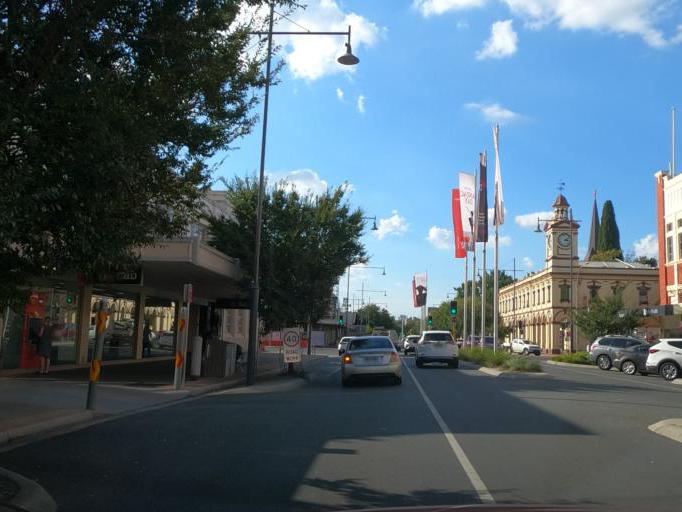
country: AU
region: New South Wales
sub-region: Albury Municipality
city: South Albury
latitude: -36.0813
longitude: 146.9155
